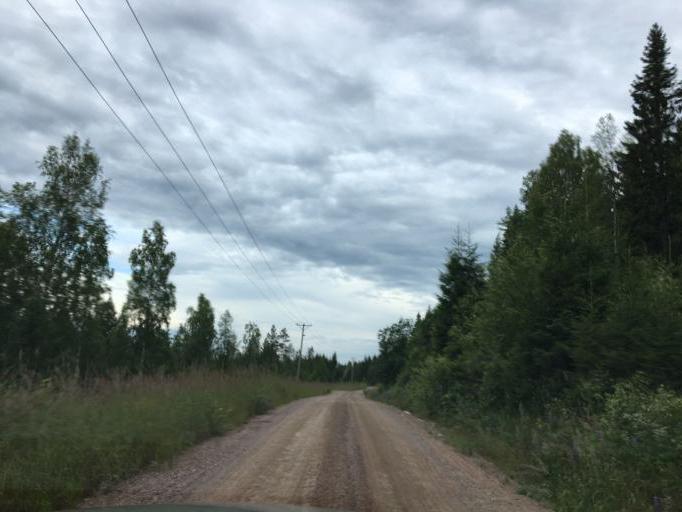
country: SE
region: Vaermland
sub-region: Filipstads Kommun
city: Lesjofors
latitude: 60.1873
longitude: 14.4002
